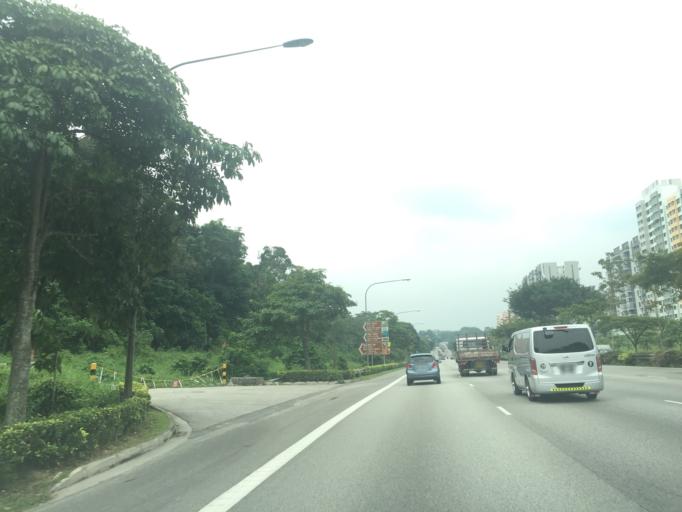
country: MY
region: Johor
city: Johor Bahru
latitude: 1.3907
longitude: 103.7664
